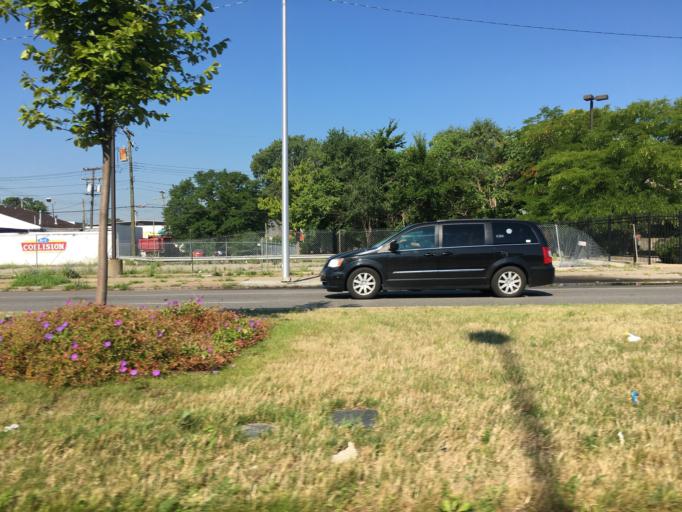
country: US
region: Michigan
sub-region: Wayne County
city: Highland Park
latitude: 42.4106
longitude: -83.1404
